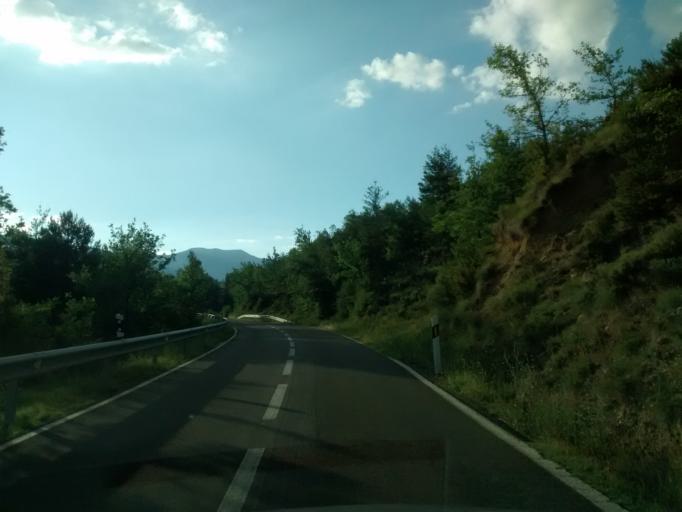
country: ES
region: Aragon
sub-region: Provincia de Huesca
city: Boltana
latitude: 42.4715
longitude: -0.0013
